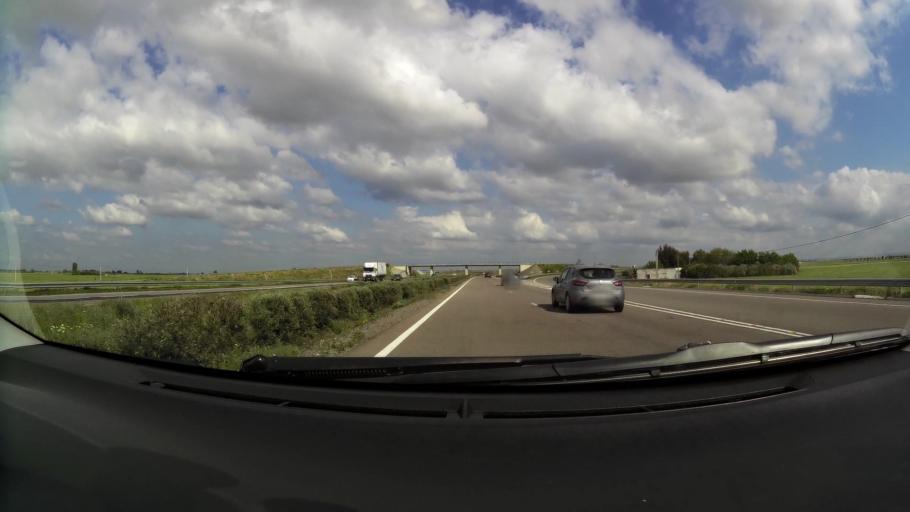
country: MA
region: Chaouia-Ouardigha
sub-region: Settat Province
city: Berrechid
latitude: 33.2996
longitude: -7.5639
